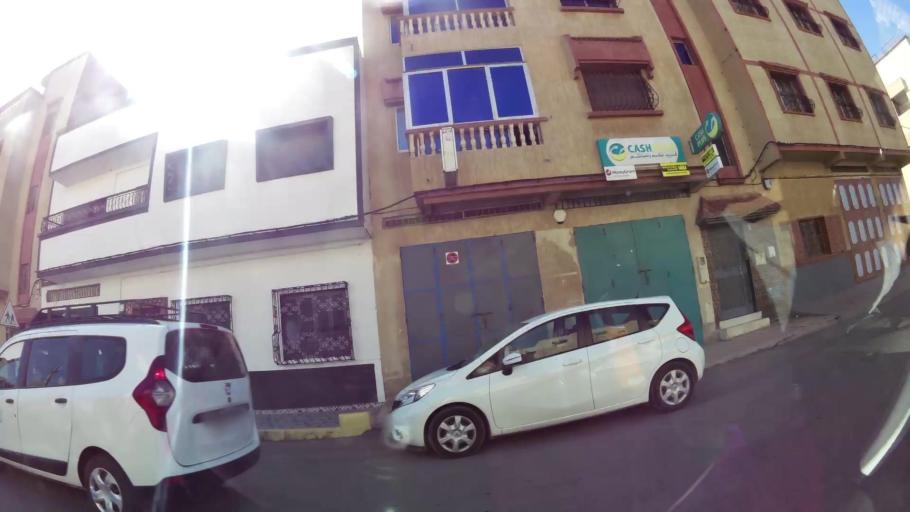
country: MA
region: Rabat-Sale-Zemmour-Zaer
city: Sale
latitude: 34.0697
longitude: -6.7982
